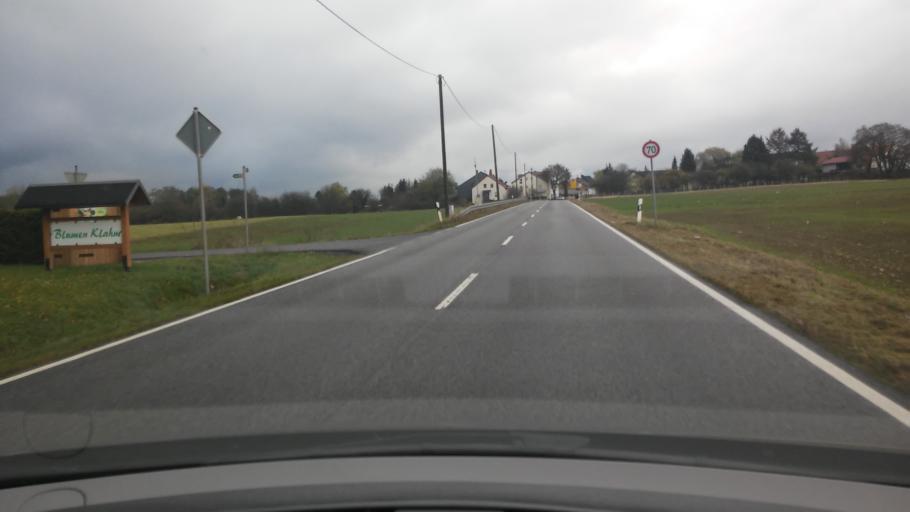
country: FR
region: Lorraine
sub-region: Departement de la Moselle
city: Merten
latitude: 49.2962
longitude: 6.6820
